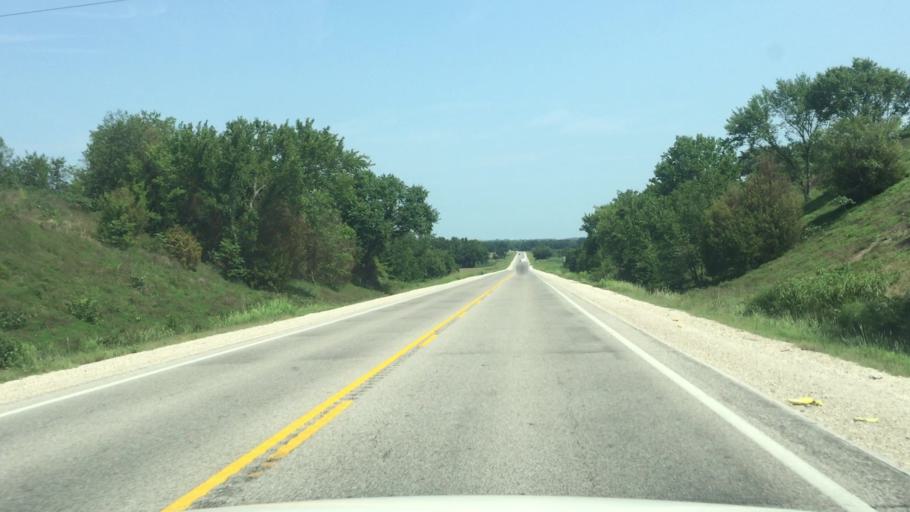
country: US
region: Kansas
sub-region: Montgomery County
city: Cherryvale
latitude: 37.1603
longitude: -95.5767
